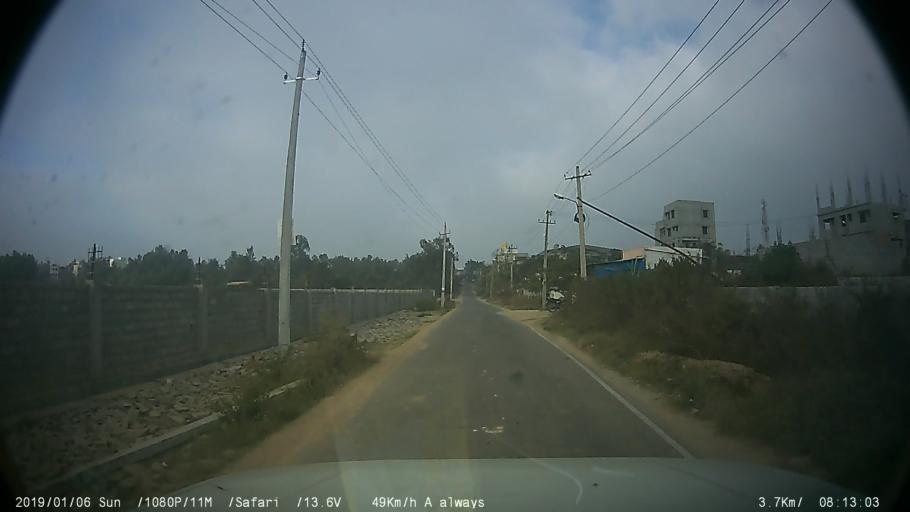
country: IN
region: Karnataka
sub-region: Bangalore Urban
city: Anekal
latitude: 12.8256
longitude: 77.6255
